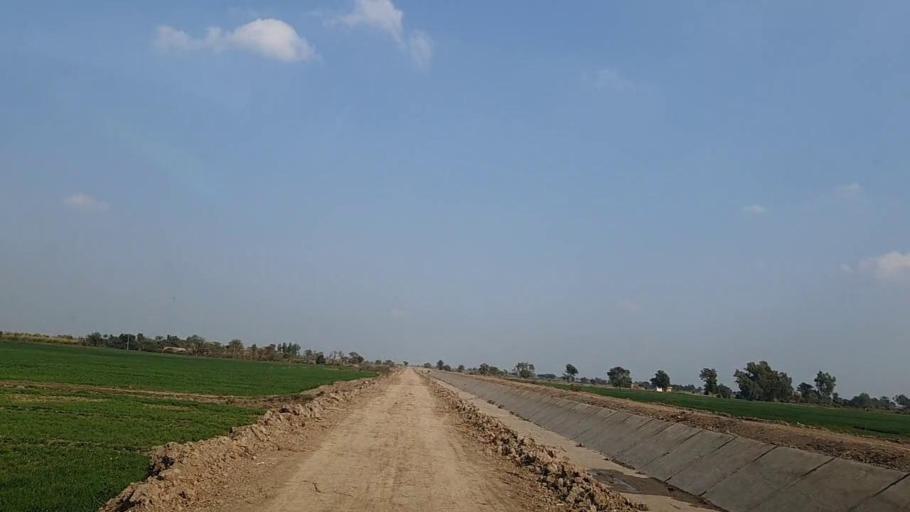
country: PK
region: Sindh
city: Nawabshah
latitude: 26.1483
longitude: 68.3794
